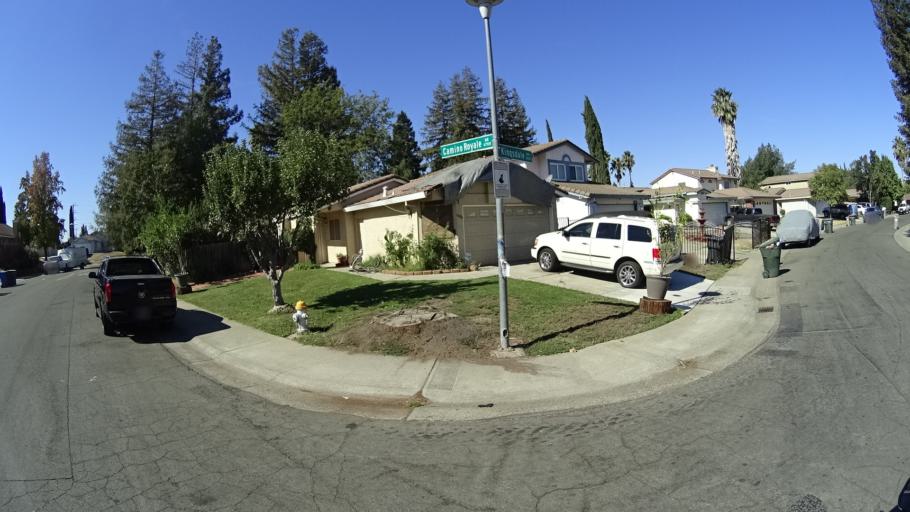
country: US
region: California
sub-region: Sacramento County
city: Parkway
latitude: 38.4641
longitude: -121.4447
